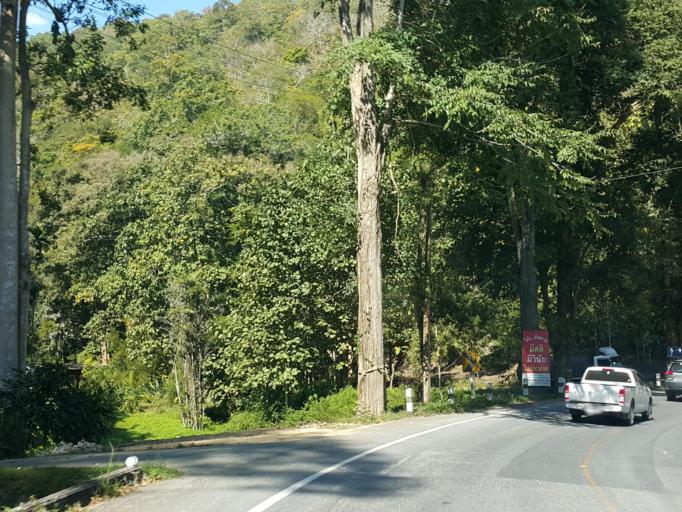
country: TH
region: Chiang Mai
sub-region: Amphoe Chiang Dao
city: Chiang Dao
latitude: 19.2702
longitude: 98.9698
